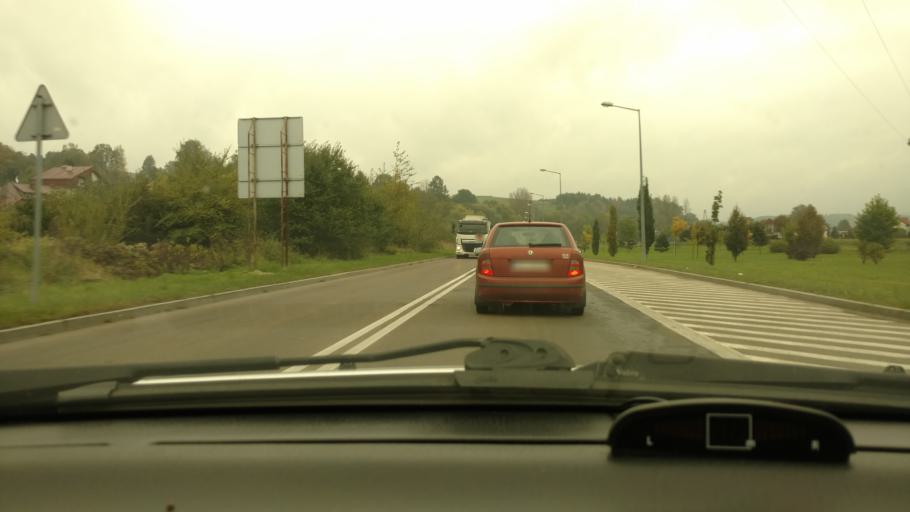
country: PL
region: Lesser Poland Voivodeship
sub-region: Powiat nowosadecki
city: Nowy Sacz
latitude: 49.6327
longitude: 20.7133
